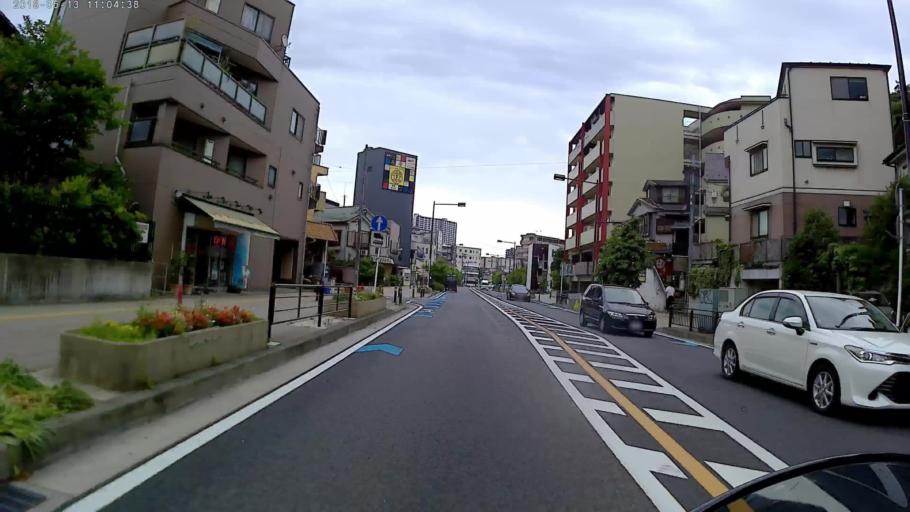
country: JP
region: Tokyo
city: Chofugaoka
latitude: 35.5982
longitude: 139.6110
